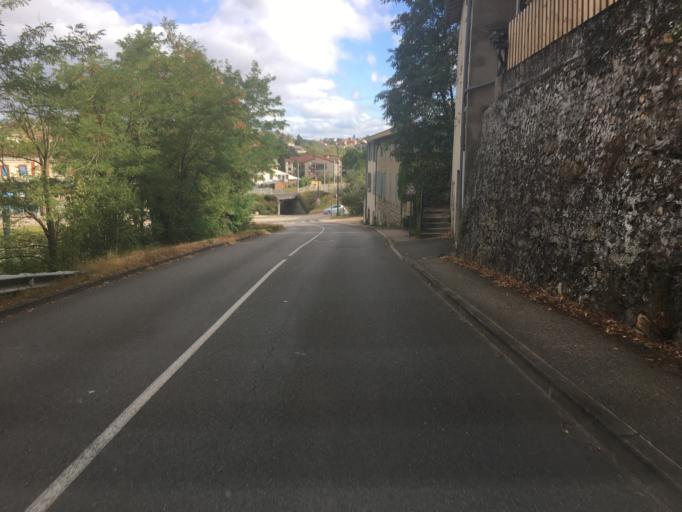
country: FR
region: Rhone-Alpes
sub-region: Departement du Rhone
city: Saint-Germain-Nuelles
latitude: 45.8320
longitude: 4.6184
